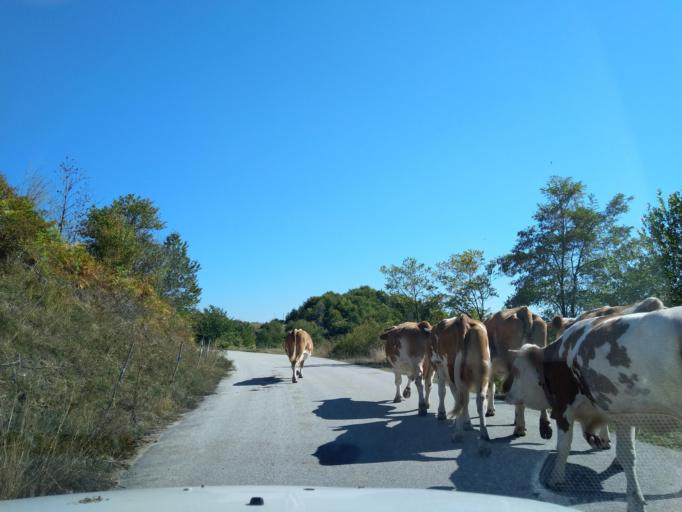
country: RS
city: Sokolovica
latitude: 43.2496
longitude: 20.3240
